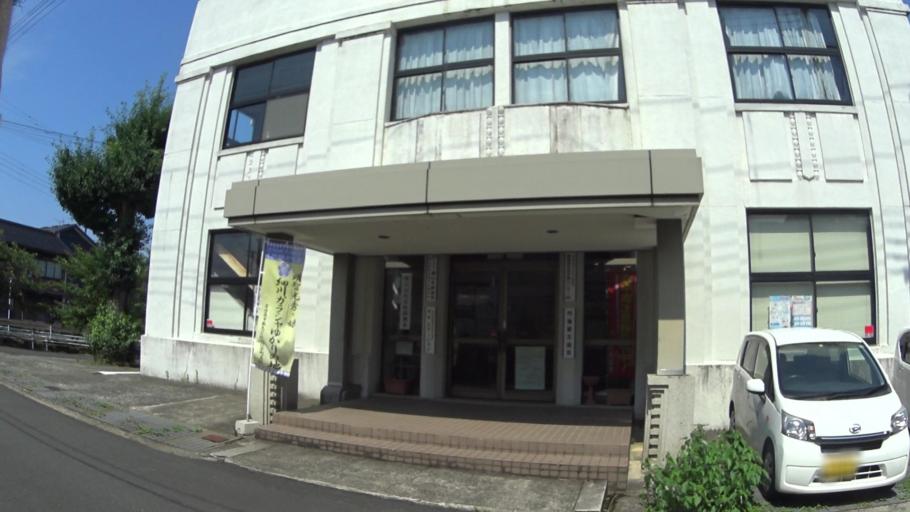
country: JP
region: Kyoto
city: Miyazu
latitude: 35.6239
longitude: 135.0599
